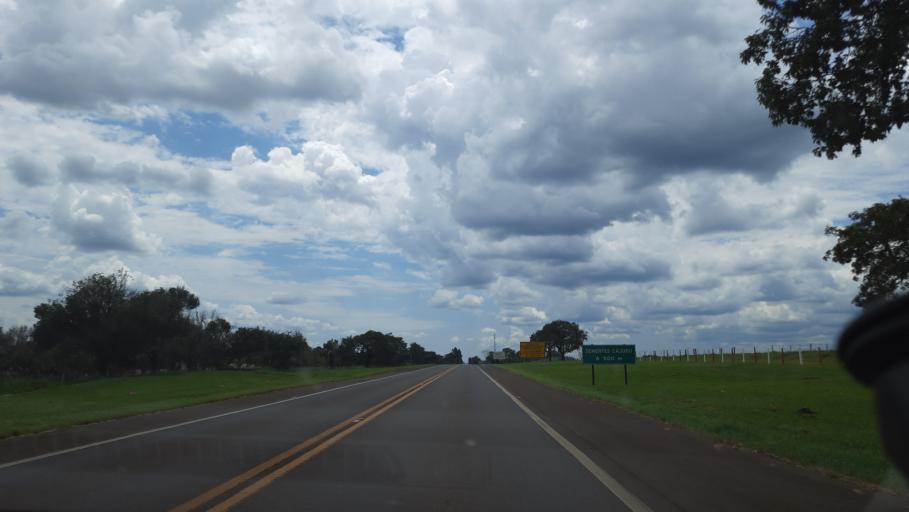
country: BR
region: Sao Paulo
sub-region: Cajuru
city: Cajuru
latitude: -21.2803
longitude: -47.2875
